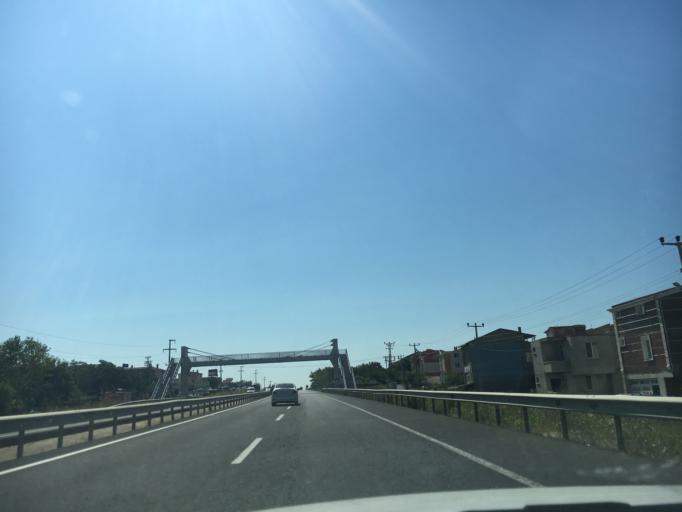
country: TR
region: Tekirdag
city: Marmara Ereglisi
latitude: 40.9774
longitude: 27.8717
